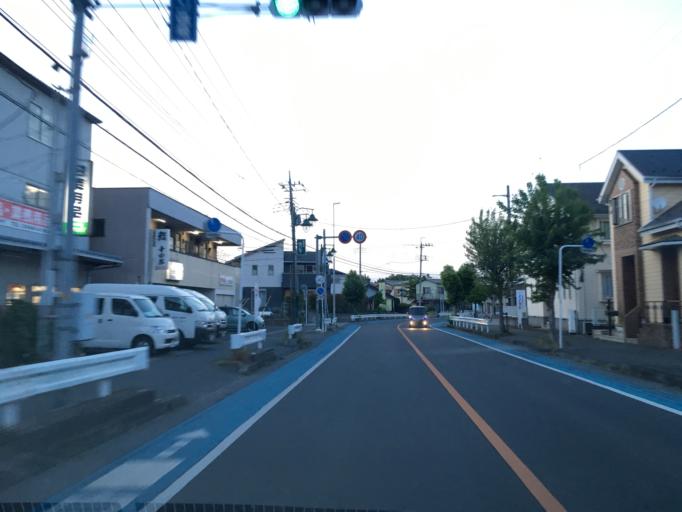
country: JP
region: Saitama
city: Sayama
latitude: 35.8466
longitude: 139.3778
